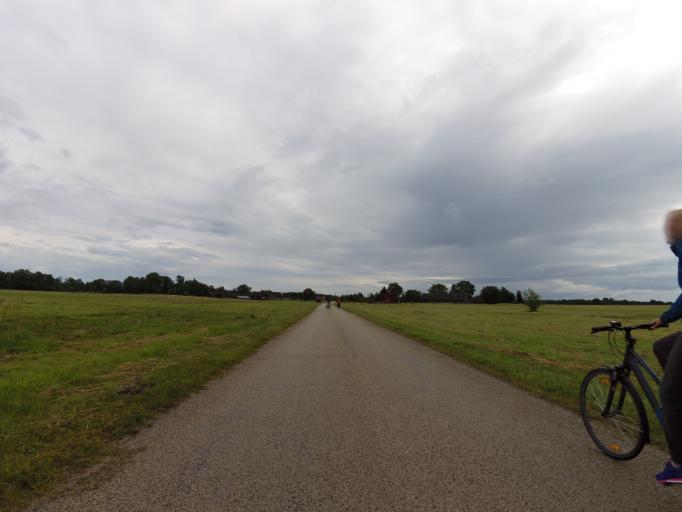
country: EE
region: Laeaene
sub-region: Vormsi vald
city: Hullo
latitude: 59.0104
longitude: 23.2794
